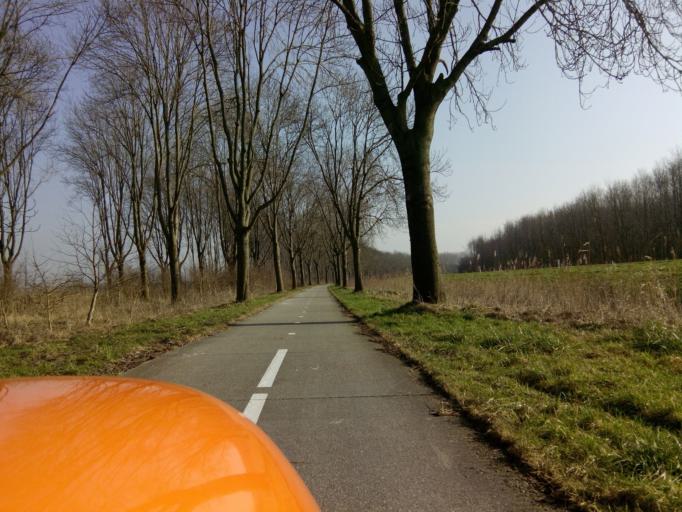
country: NL
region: Utrecht
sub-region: Gemeente Bunschoten
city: Bunschoten
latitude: 52.2812
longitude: 5.4351
